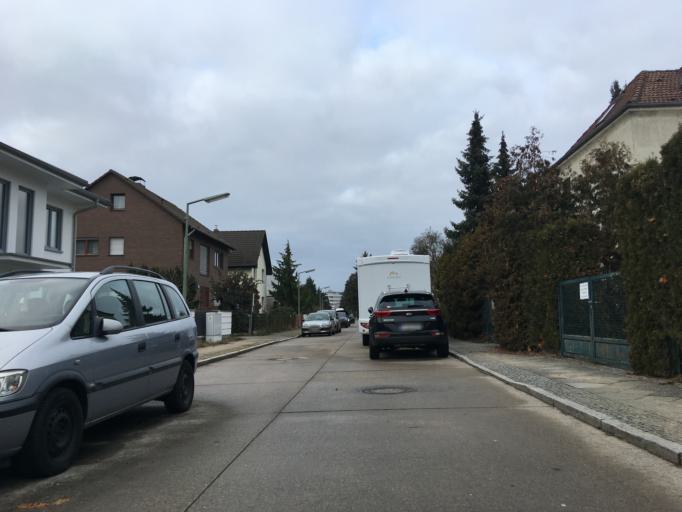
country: DE
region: Berlin
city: Wittenau
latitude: 52.5917
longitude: 13.3388
